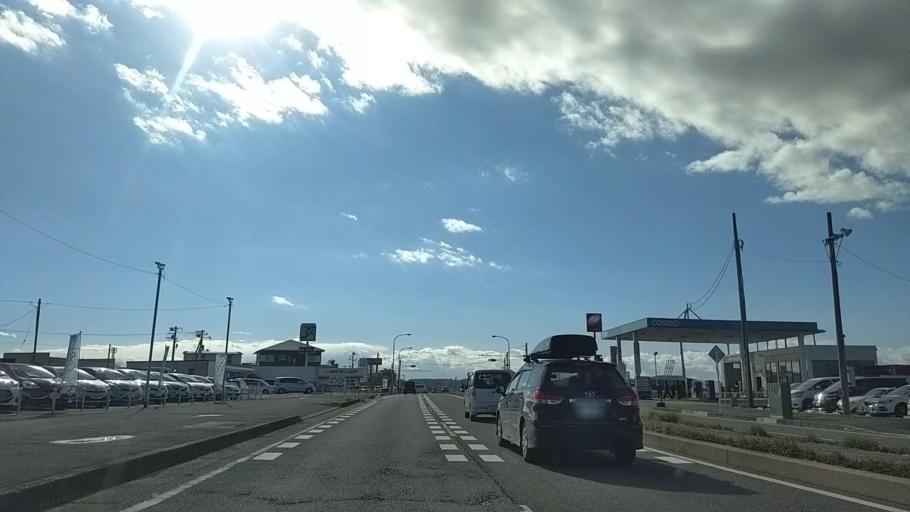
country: JP
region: Chiba
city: Tateyama
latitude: 35.0168
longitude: 139.8718
